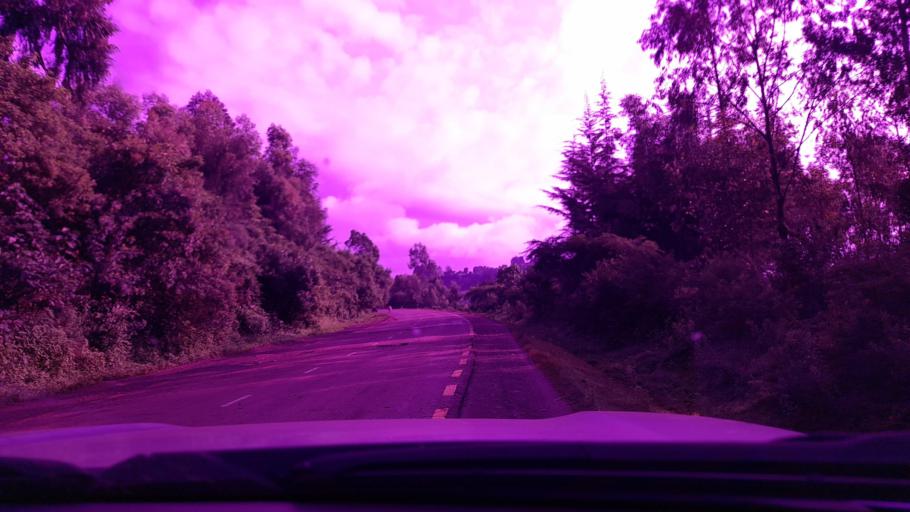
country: ET
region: Oromiya
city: Bedele
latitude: 8.2115
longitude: 36.4453
